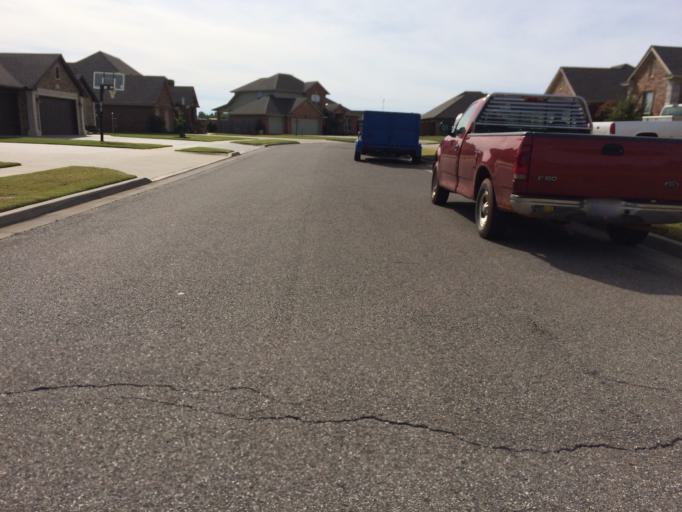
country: US
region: Oklahoma
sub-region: Cleveland County
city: Norman
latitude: 35.2371
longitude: -97.4359
